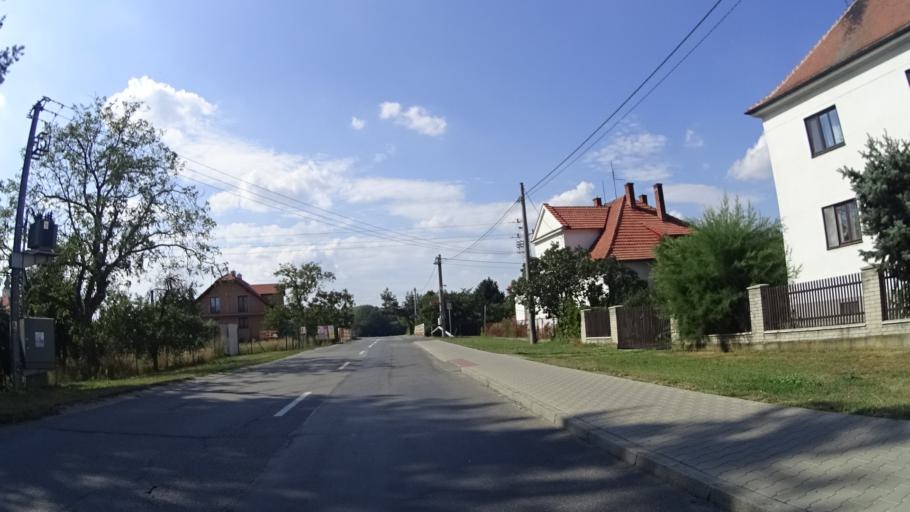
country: CZ
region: Zlin
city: Uhersky Ostroh
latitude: 48.9863
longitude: 17.3948
